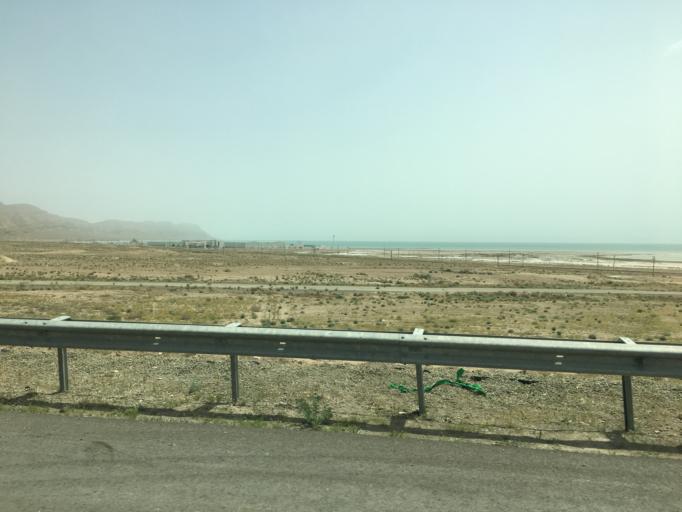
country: TM
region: Balkan
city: Turkmenbasy
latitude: 40.0112
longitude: 53.1509
